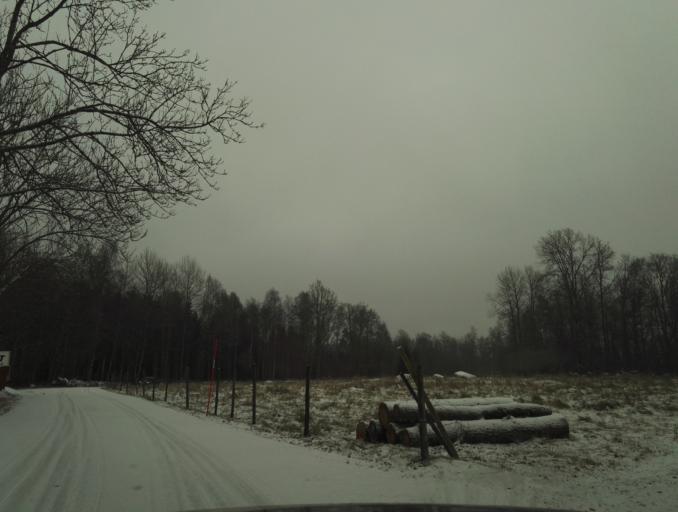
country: SE
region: Kronoberg
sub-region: Alvesta Kommun
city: Vislanda
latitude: 56.6960
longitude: 14.4165
